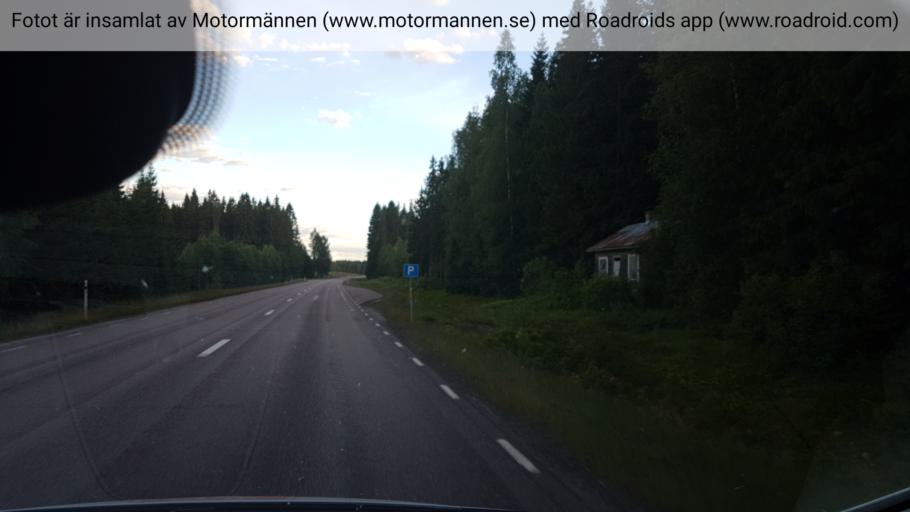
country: SE
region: Vaermland
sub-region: Torsby Kommun
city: Torsby
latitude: 60.0509
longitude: 13.0651
